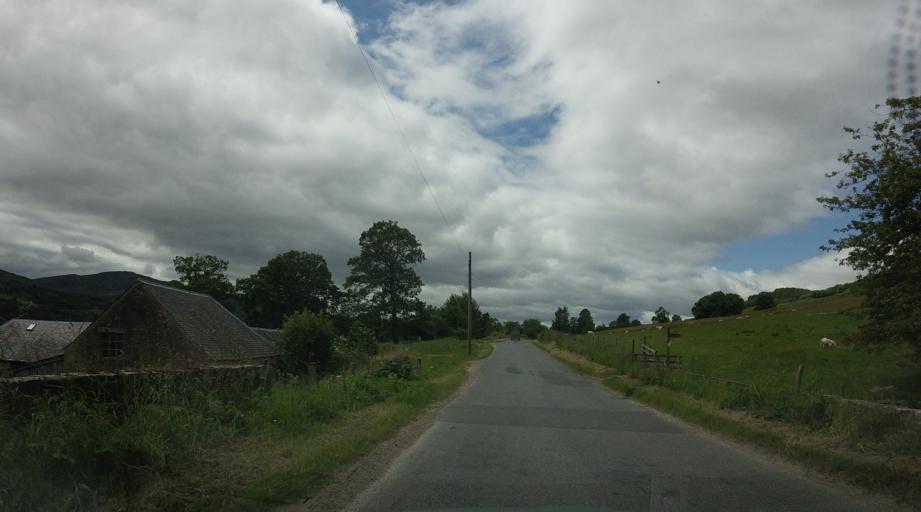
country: GB
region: Scotland
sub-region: Perth and Kinross
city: Aberfeldy
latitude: 56.7183
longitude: -3.8995
